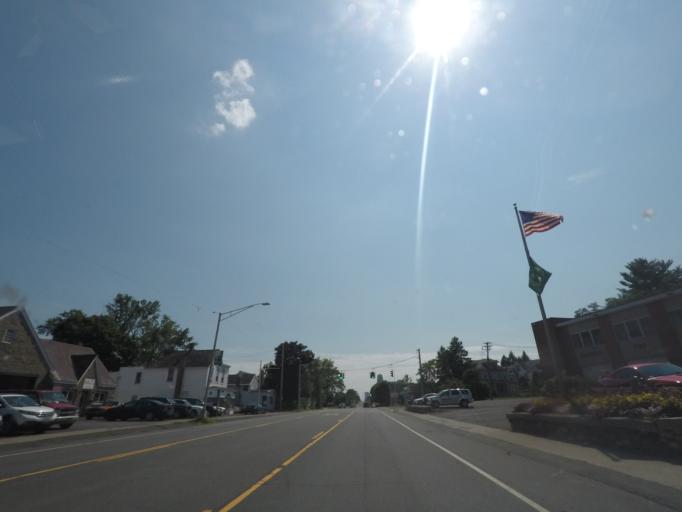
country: US
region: New York
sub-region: Albany County
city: Menands
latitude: 42.6924
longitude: -73.7243
